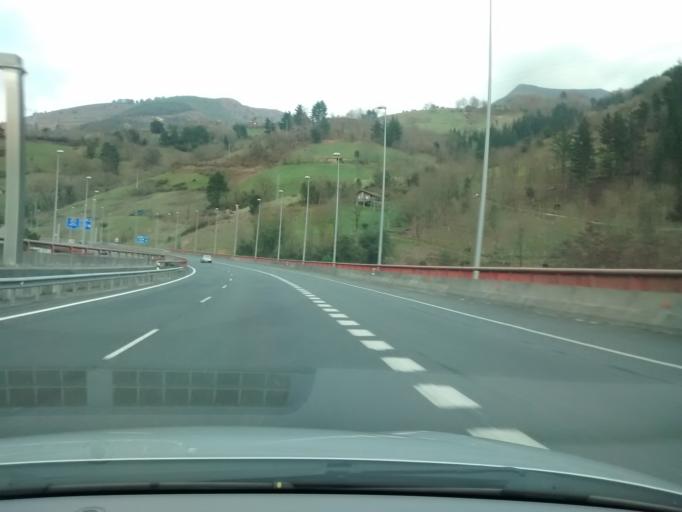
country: ES
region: Basque Country
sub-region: Bizkaia
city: Gordexola
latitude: 43.1946
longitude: -3.0442
